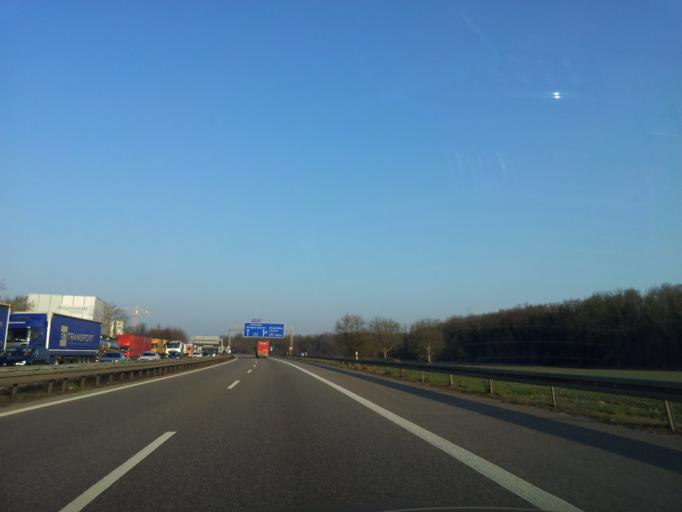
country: FR
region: Alsace
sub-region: Departement du Haut-Rhin
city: Huningue
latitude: 47.6074
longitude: 7.5982
